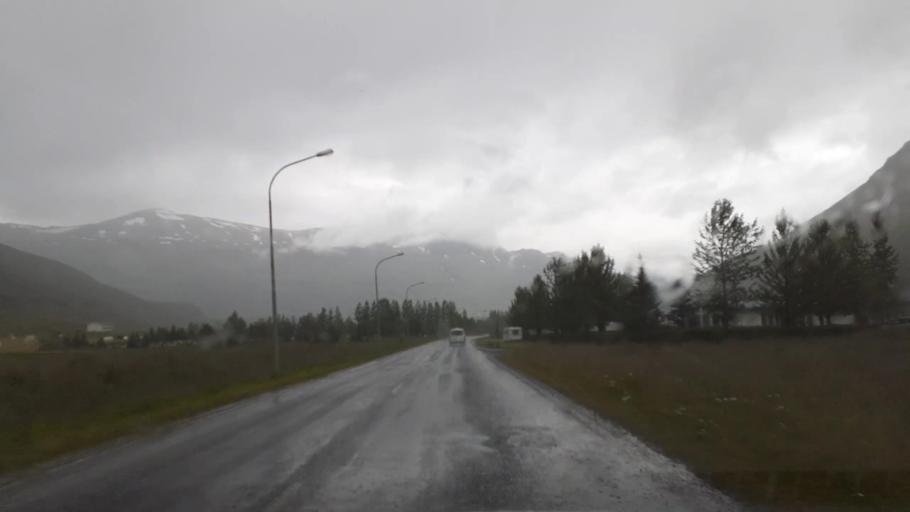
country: IS
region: East
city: Eskifjoerdur
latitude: 65.2526
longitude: -14.0168
